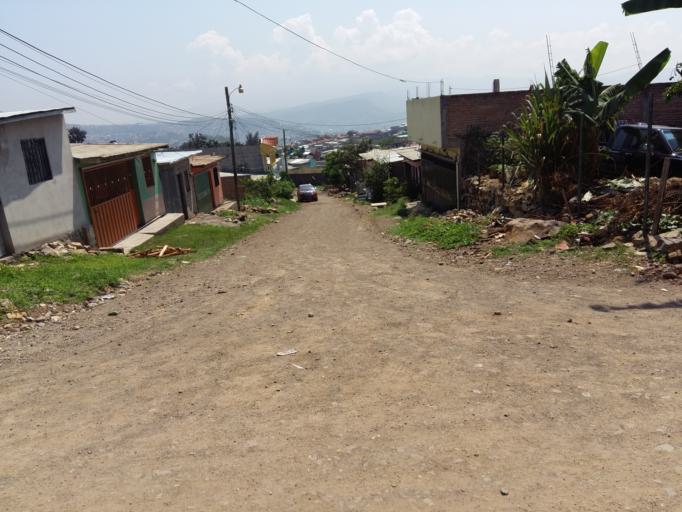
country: HN
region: Francisco Morazan
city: Tegucigalpa
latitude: 14.0793
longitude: -87.2467
